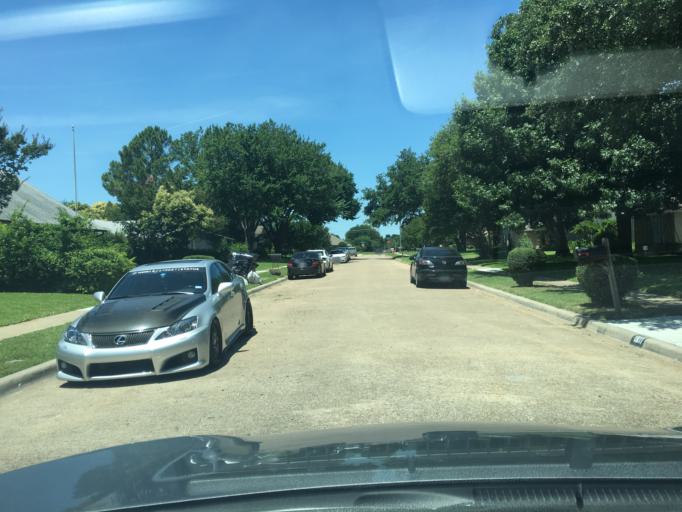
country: US
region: Texas
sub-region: Dallas County
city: Richardson
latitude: 32.9411
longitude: -96.6897
